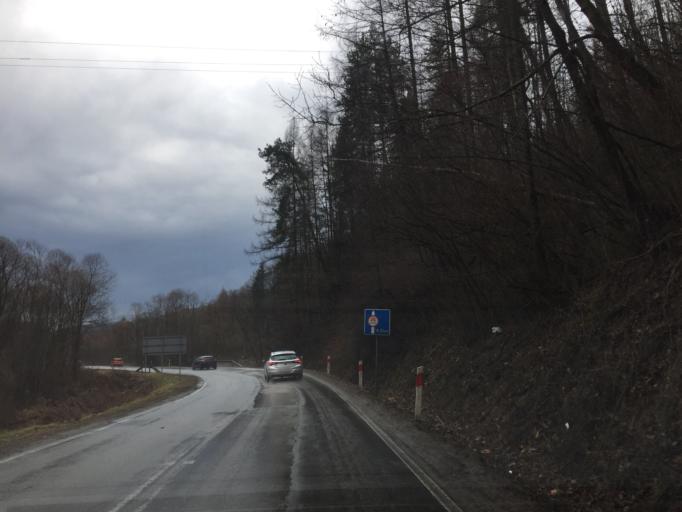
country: PL
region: Lesser Poland Voivodeship
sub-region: Powiat suski
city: Zembrzyce
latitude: 49.7714
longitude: 19.6160
